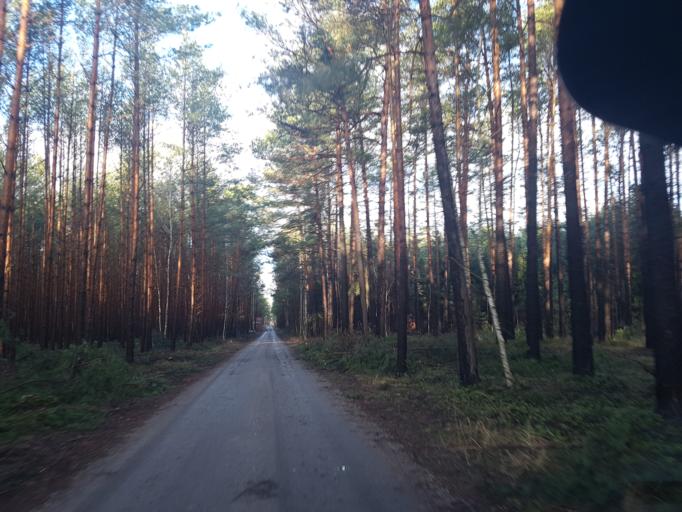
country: DE
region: Brandenburg
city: Ruckersdorf
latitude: 51.5864
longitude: 13.5959
